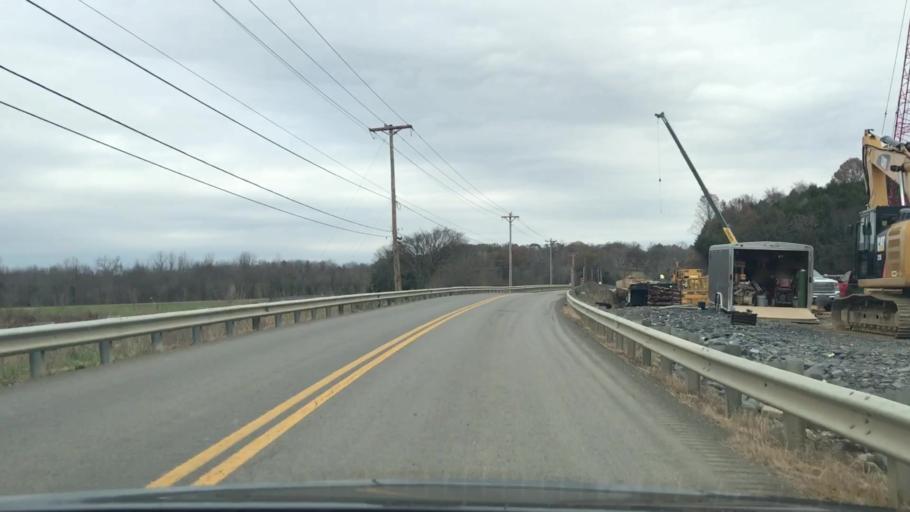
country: US
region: Kentucky
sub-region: Metcalfe County
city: Edmonton
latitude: 36.9296
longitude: -85.6400
